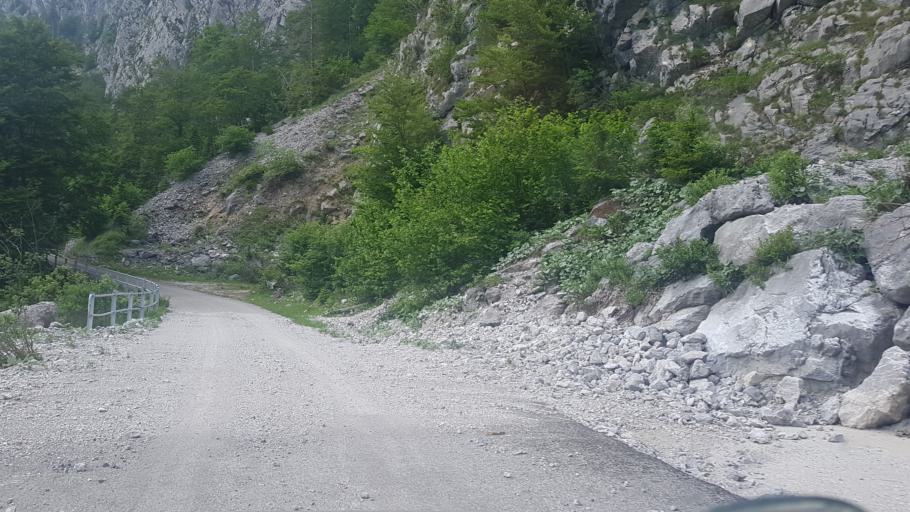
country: IT
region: Friuli Venezia Giulia
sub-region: Provincia di Udine
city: Paularo
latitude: 46.5497
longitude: 13.2026
